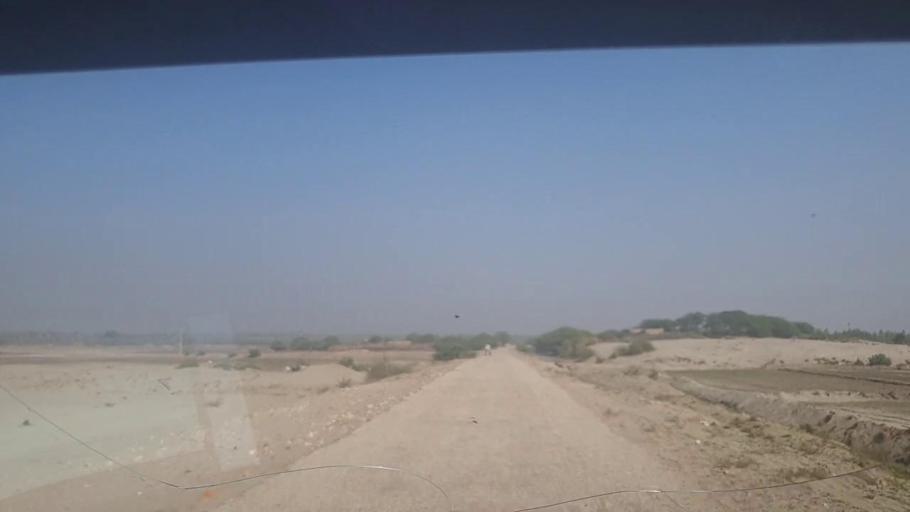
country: PK
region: Sindh
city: Khairpur
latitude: 27.4512
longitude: 68.7212
